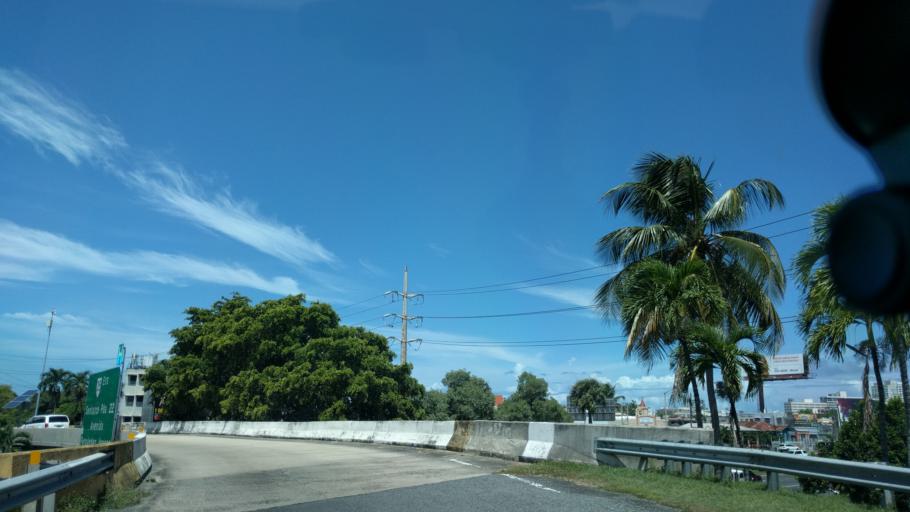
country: PR
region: San Juan
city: San Juan
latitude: 18.4412
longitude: -66.0701
